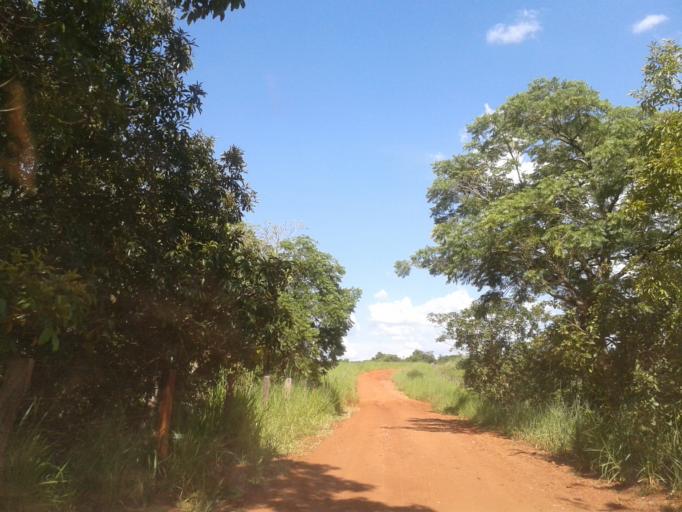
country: BR
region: Minas Gerais
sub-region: Santa Vitoria
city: Santa Vitoria
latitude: -19.1199
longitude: -50.4289
